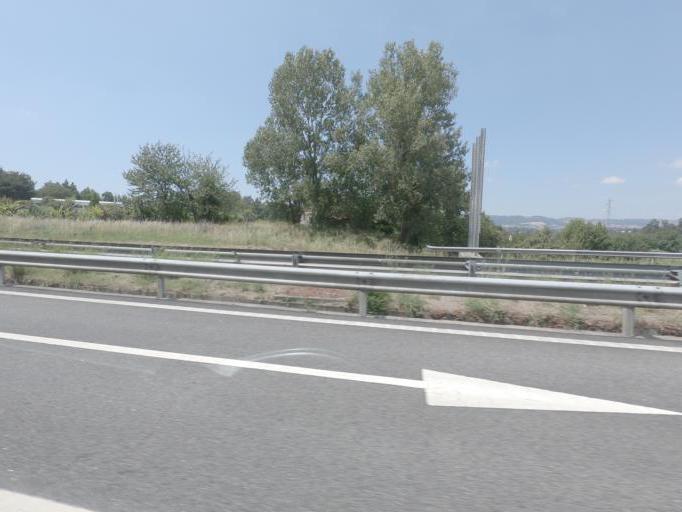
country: PT
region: Porto
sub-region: Penafiel
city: Penafiel
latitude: 41.2095
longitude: -8.2905
